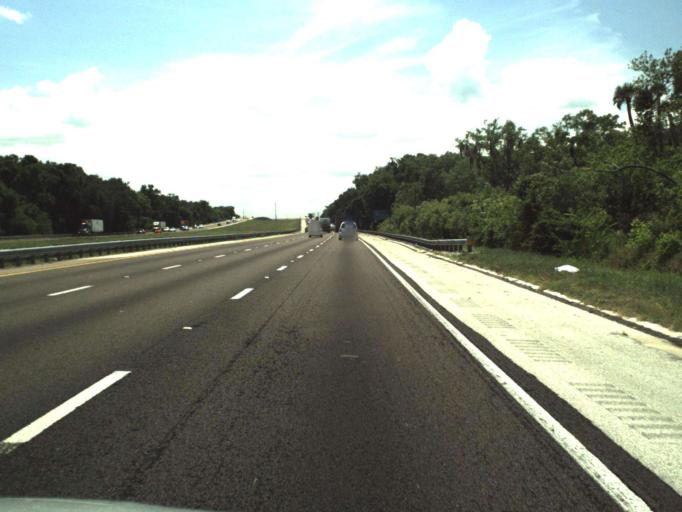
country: US
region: Florida
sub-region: Volusia County
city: DeBary
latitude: 28.8439
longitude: -81.3111
